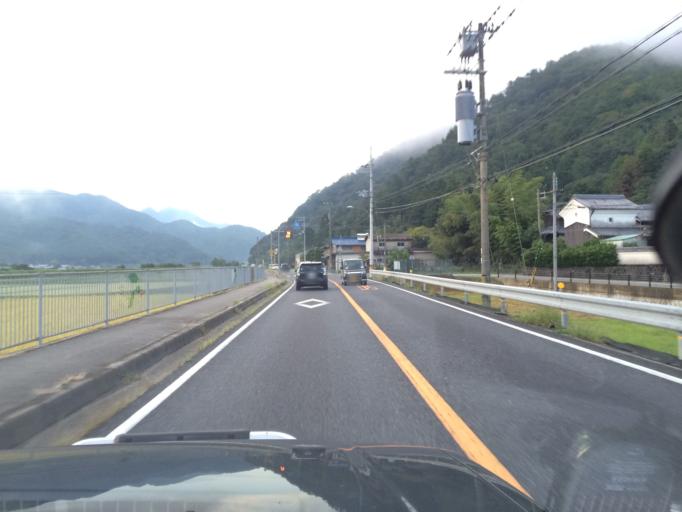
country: JP
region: Hyogo
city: Nishiwaki
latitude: 35.1234
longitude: 135.0073
